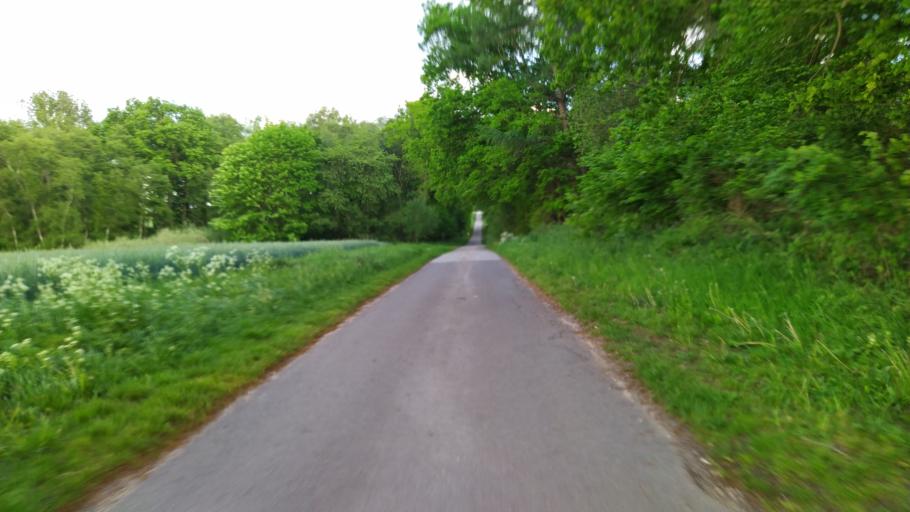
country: DE
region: Lower Saxony
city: Bargstedt
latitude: 53.4739
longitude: 9.4617
